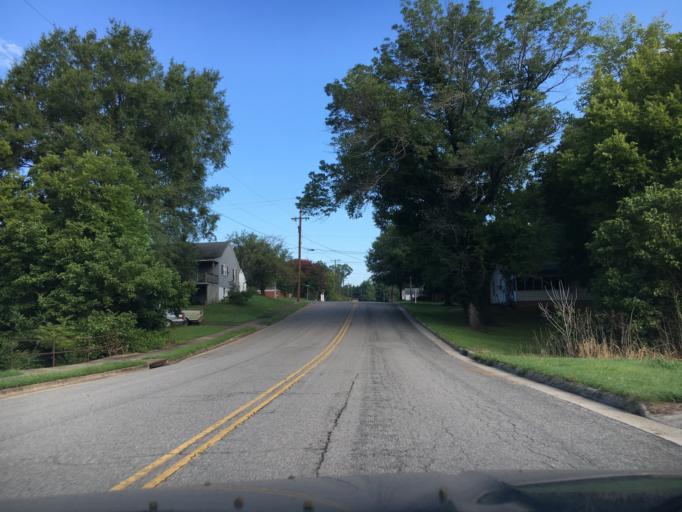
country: US
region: Virginia
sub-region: Halifax County
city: South Boston
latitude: 36.7022
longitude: -78.9104
